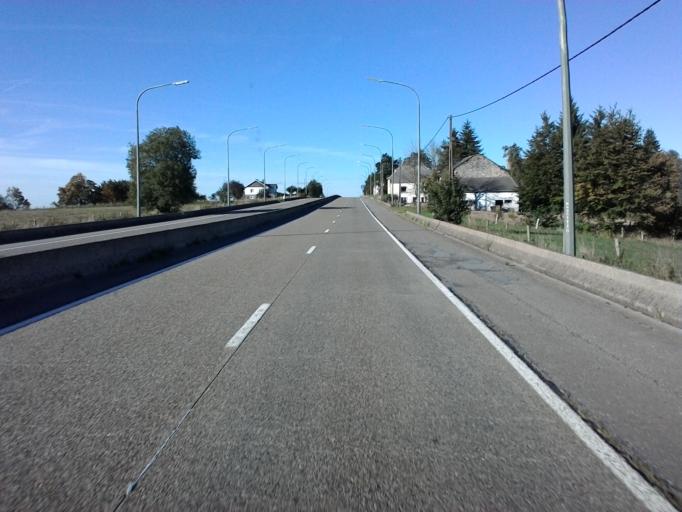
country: BE
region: Wallonia
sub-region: Province du Luxembourg
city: Fauvillers
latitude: 49.9201
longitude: 5.7037
